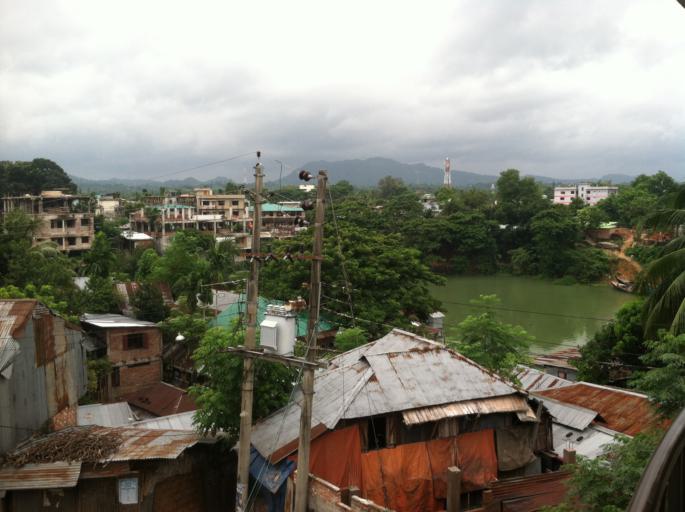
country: BD
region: Chittagong
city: Raojan
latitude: 22.6586
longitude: 92.1745
